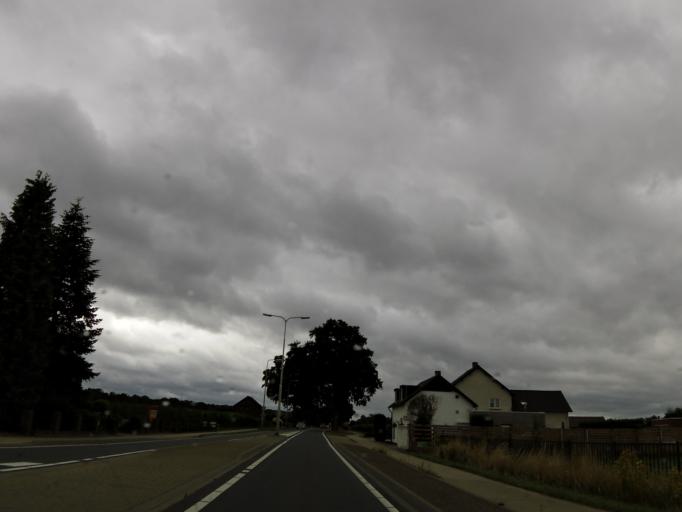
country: NL
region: Limburg
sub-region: Gemeente Maasgouw
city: Maasbracht
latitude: 51.0881
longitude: 5.8784
